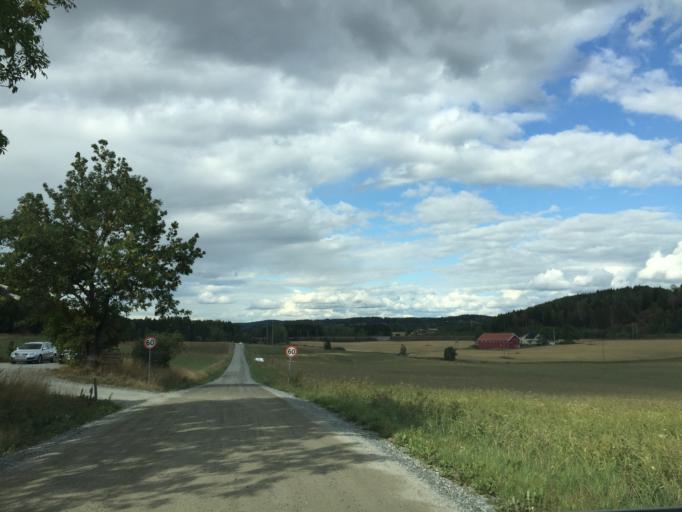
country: NO
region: Ostfold
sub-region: Askim
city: Askim
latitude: 59.5958
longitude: 11.1344
